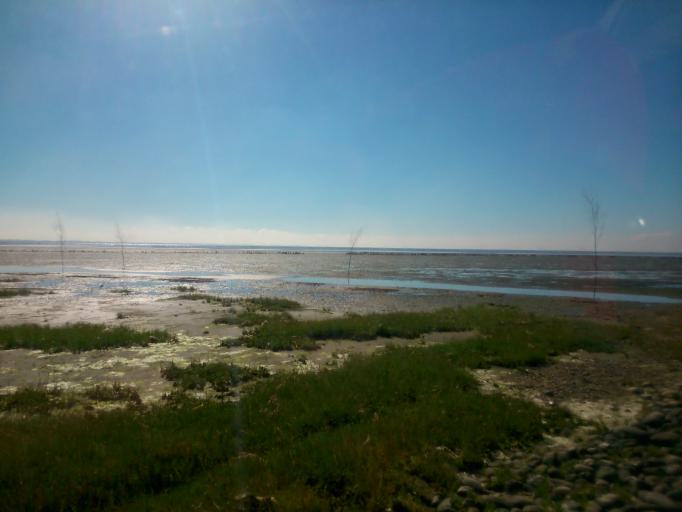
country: DK
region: South Denmark
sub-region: Esbjerg Kommune
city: Ribe
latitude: 55.2951
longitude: 8.6046
